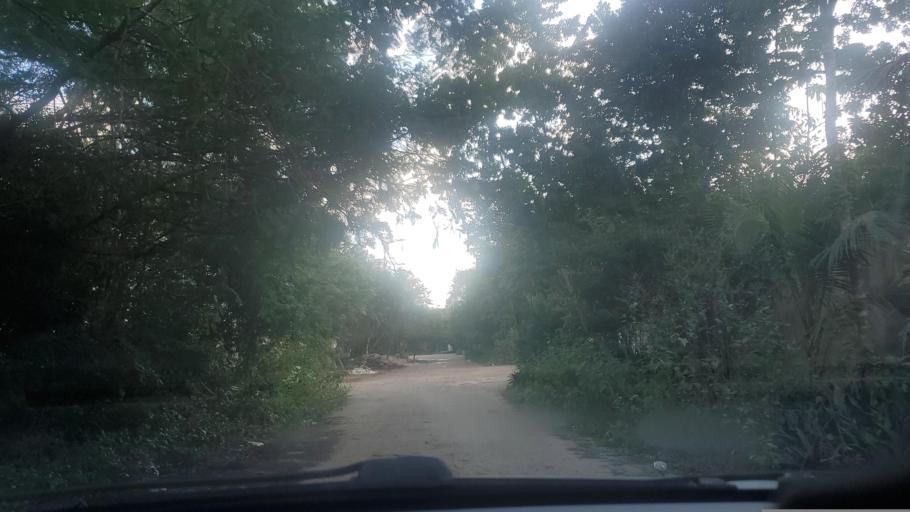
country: MX
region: Quintana Roo
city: Tulum
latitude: 20.2086
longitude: -87.4777
